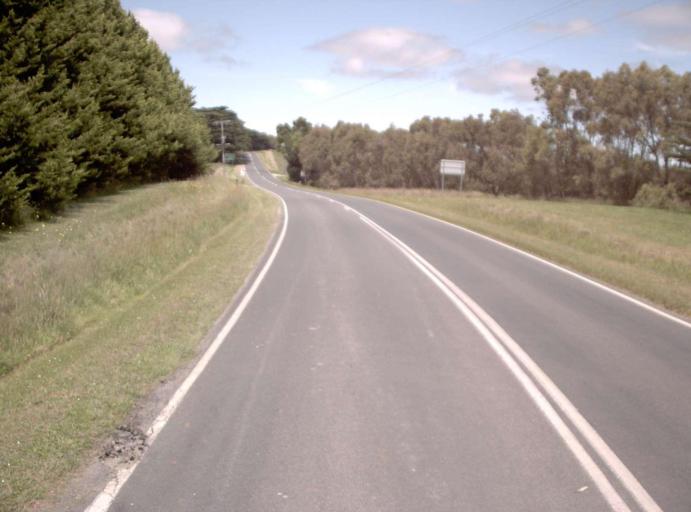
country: AU
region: Victoria
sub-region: Bass Coast
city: North Wonthaggi
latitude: -38.7027
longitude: 146.0871
